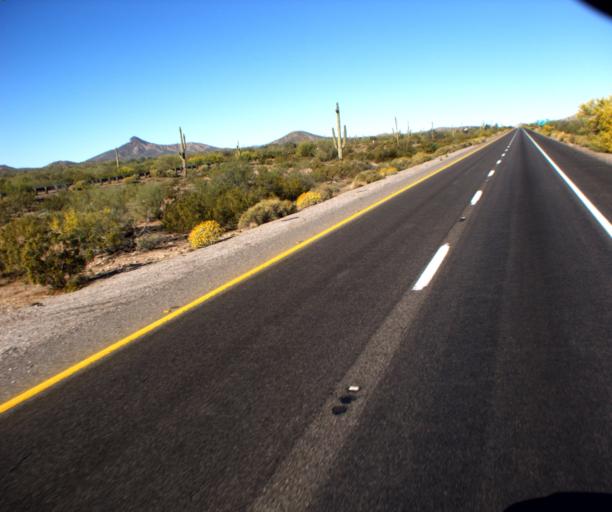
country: US
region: Arizona
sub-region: Pinal County
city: Maricopa
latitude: 32.8339
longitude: -112.1074
